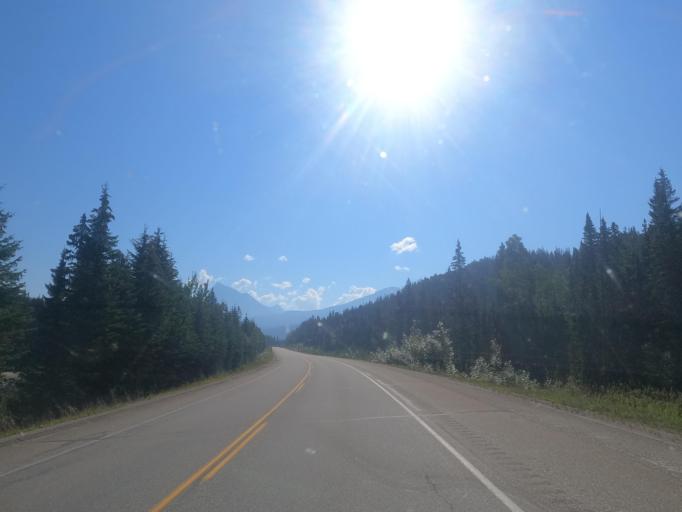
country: CA
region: Alberta
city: Jasper Park Lodge
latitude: 52.8596
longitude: -118.6380
